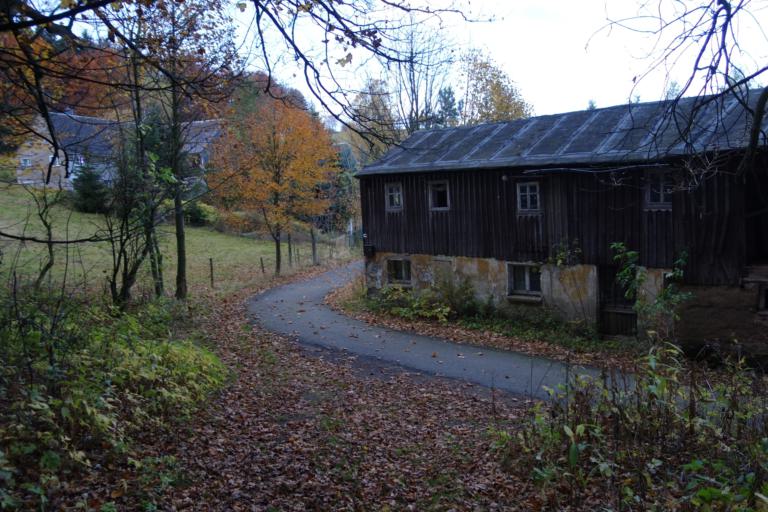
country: DE
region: Saxony
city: Rechenberg-Bienenmuhle
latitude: 50.7318
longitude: 13.5253
